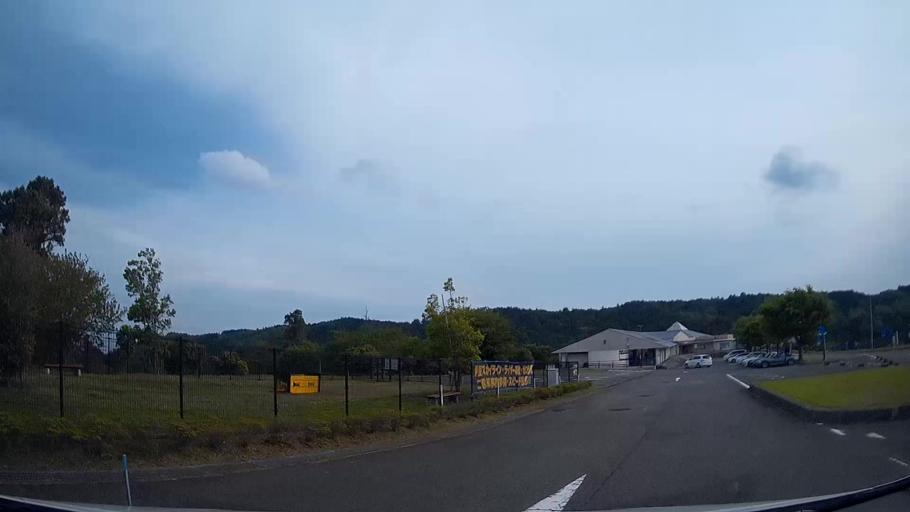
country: JP
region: Shizuoka
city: Atami
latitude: 35.0249
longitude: 139.0441
